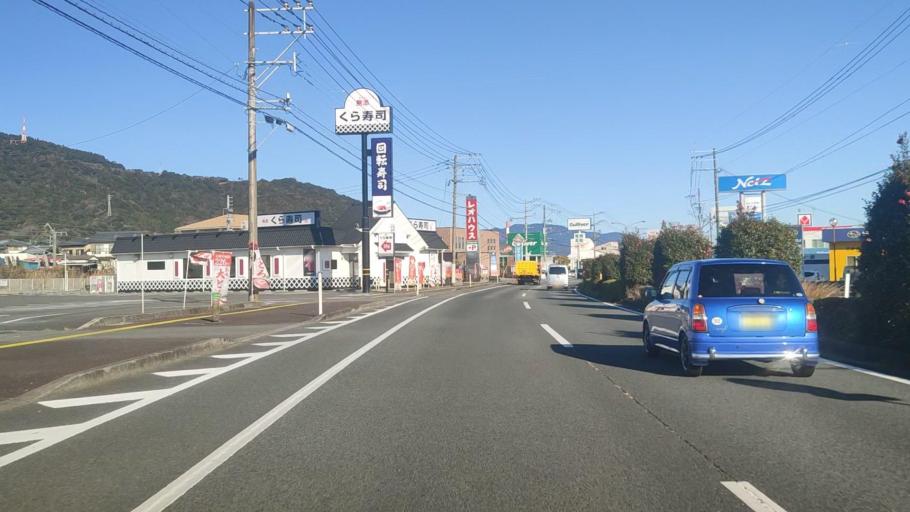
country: JP
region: Miyazaki
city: Nobeoka
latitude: 32.5477
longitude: 131.6772
